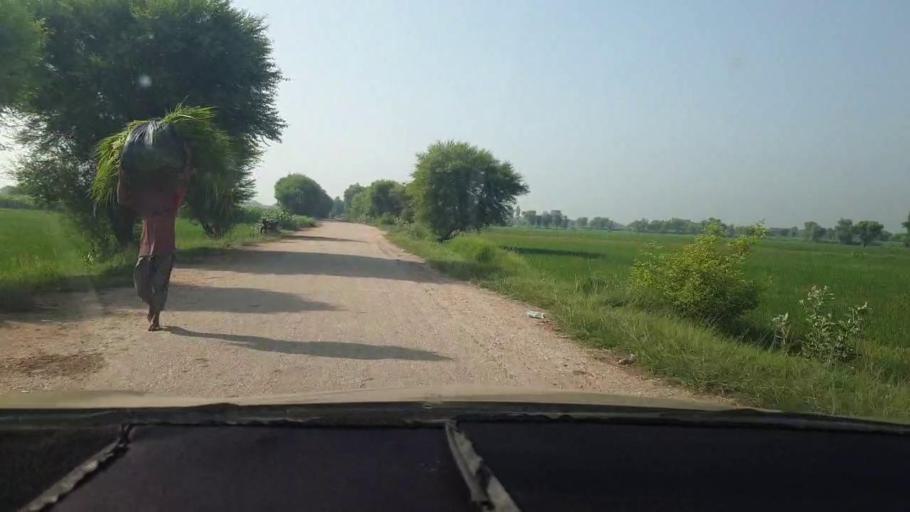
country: PK
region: Sindh
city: Kambar
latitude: 27.6172
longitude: 68.0904
